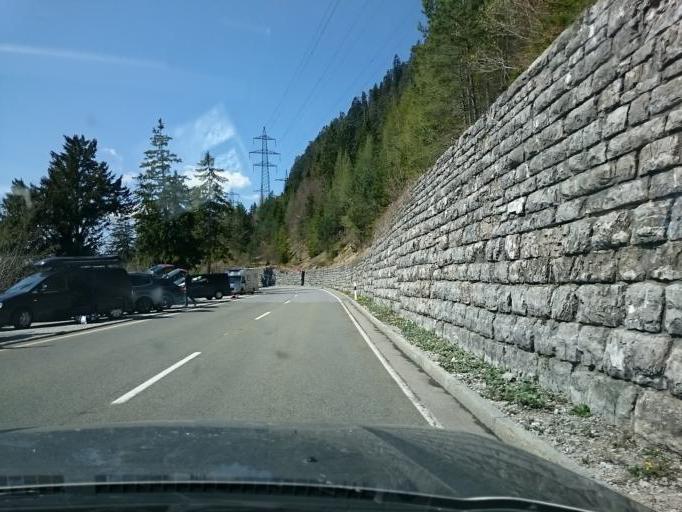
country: DE
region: Bavaria
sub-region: Upper Bavaria
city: Schlehdorf
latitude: 47.6031
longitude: 11.3321
